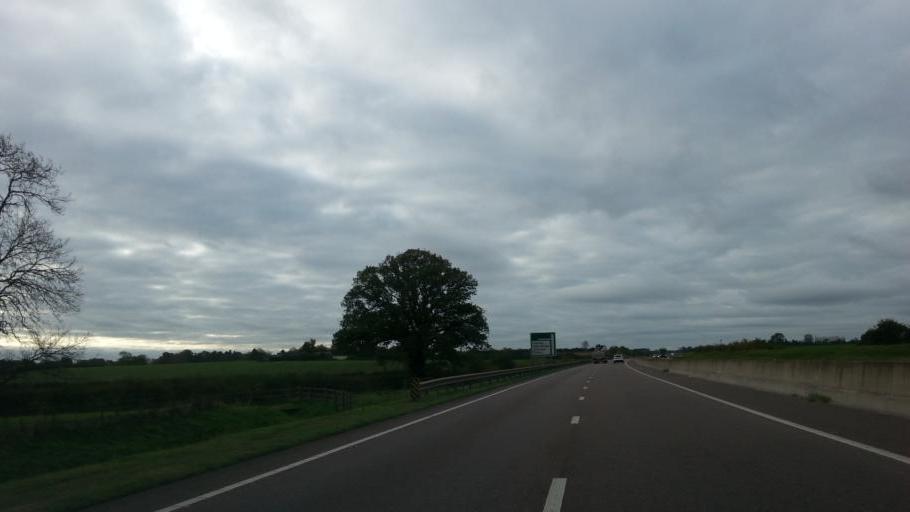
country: GB
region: England
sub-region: Nottinghamshire
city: Farndon
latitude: 53.0352
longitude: -0.8719
